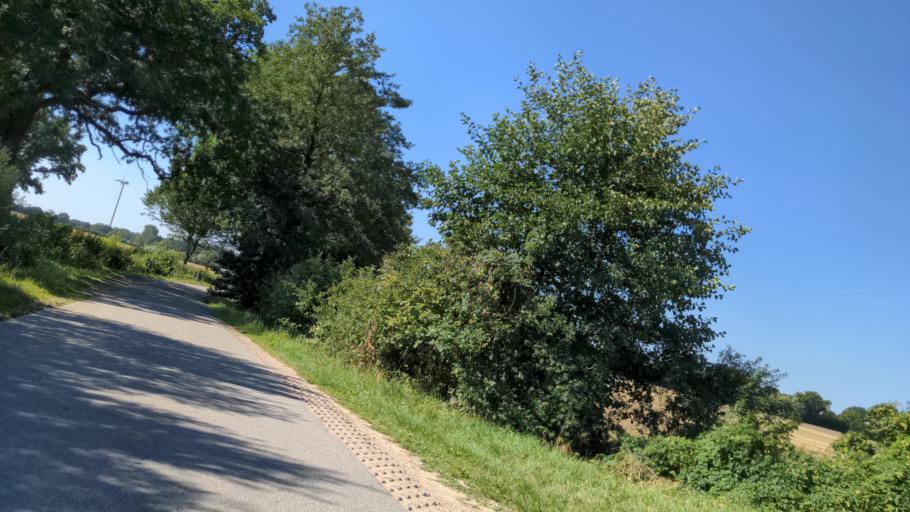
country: DE
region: Schleswig-Holstein
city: Grinau
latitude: 53.7731
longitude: 10.5641
